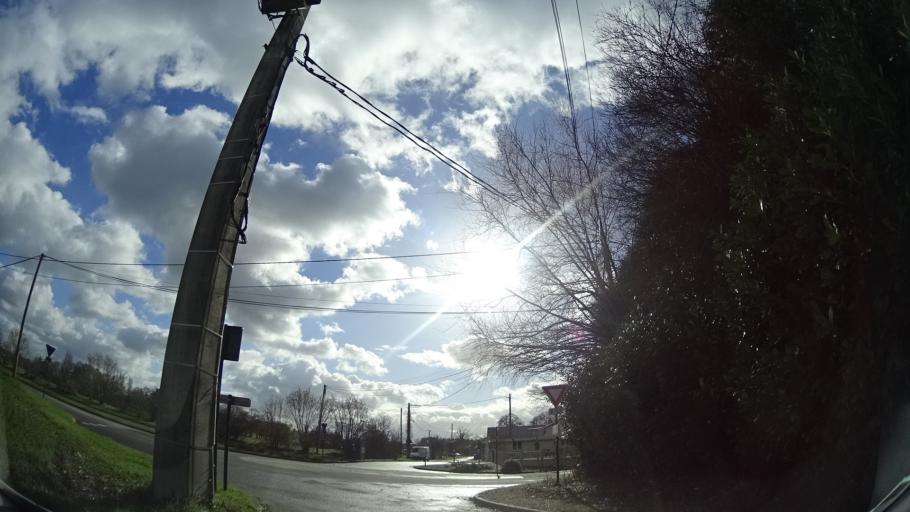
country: FR
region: Brittany
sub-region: Departement d'Ille-et-Vilaine
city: Chantepie
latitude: 48.0757
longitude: -1.6416
